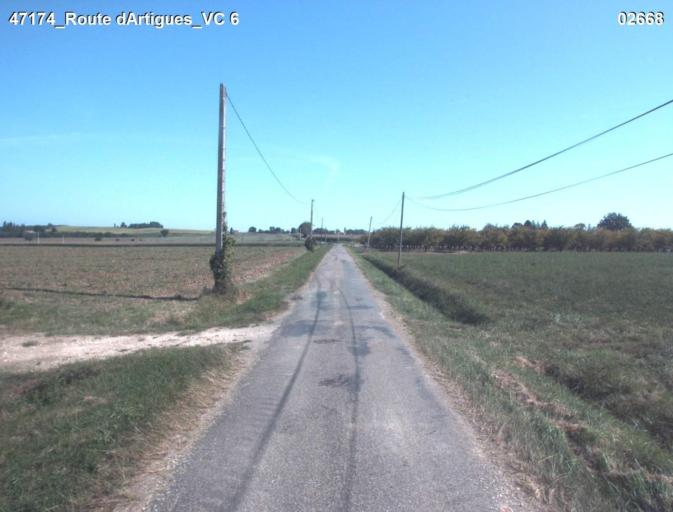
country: FR
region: Aquitaine
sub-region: Departement du Lot-et-Garonne
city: Mezin
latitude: 44.0305
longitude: 0.3348
